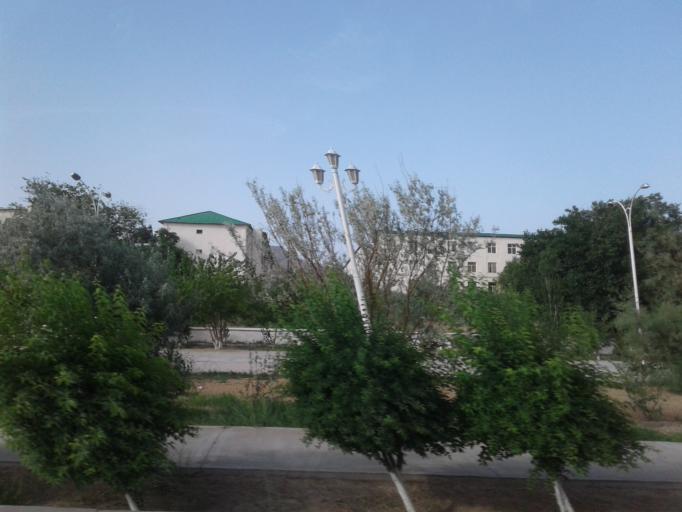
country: TM
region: Balkan
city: Turkmenbasy
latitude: 40.0006
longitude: 52.9573
